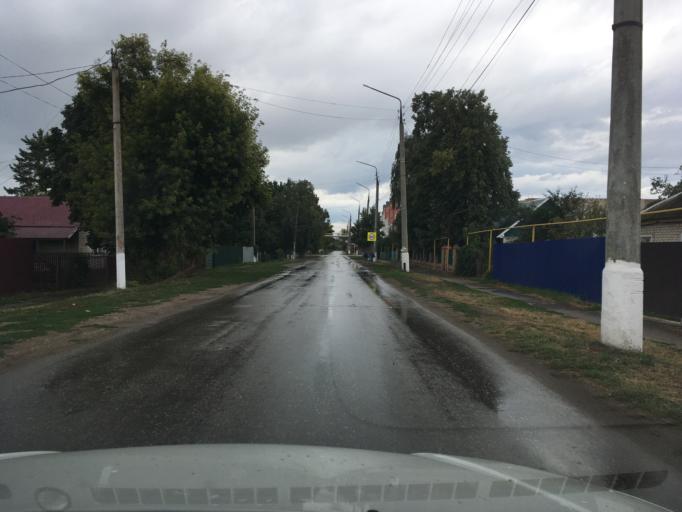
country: RU
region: Samara
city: Bezenchuk
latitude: 52.9825
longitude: 49.4393
